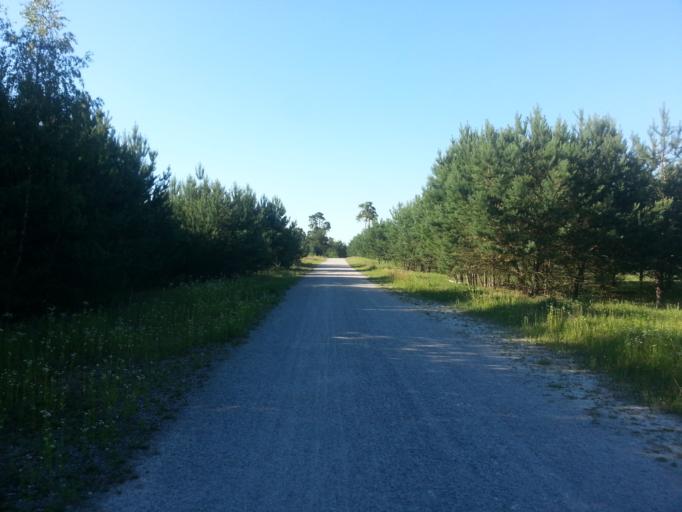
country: DE
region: Hesse
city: Viernheim
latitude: 49.5360
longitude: 8.5456
